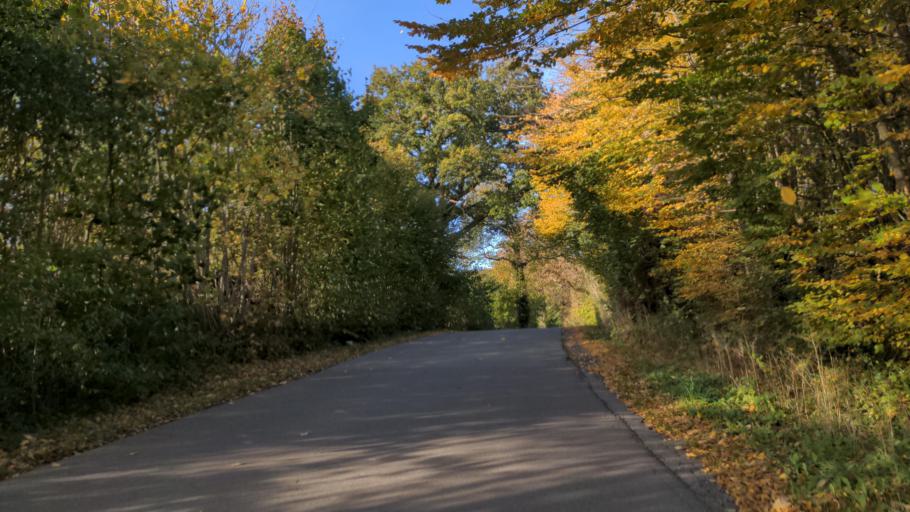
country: DE
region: Schleswig-Holstein
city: Kirchnuchel
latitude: 54.1884
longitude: 10.6757
